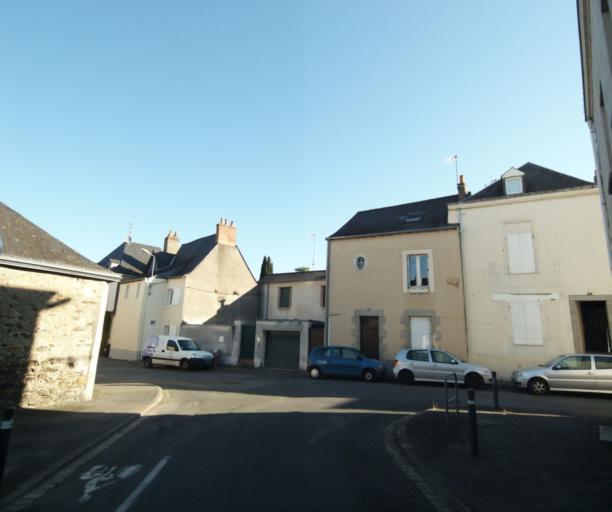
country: FR
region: Pays de la Loire
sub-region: Departement de la Mayenne
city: Laval
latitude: 48.0645
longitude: -0.7641
